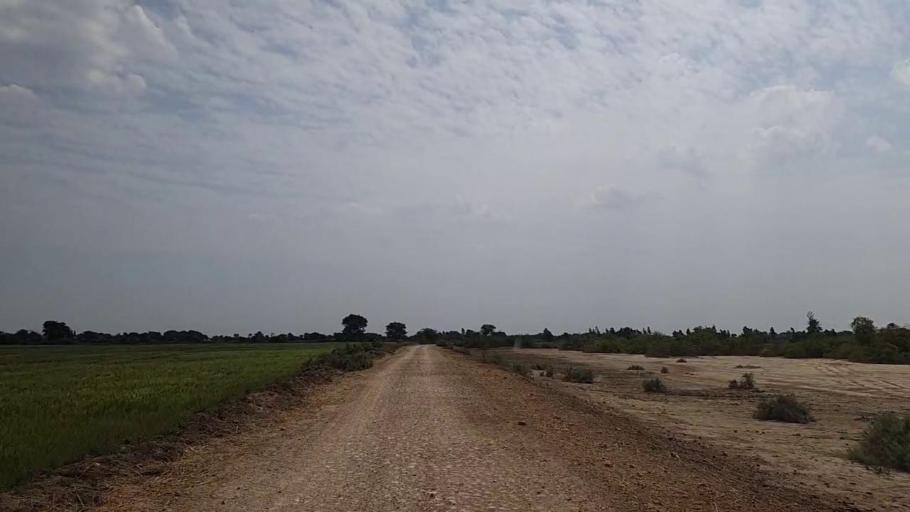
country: PK
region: Sindh
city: Daro Mehar
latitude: 24.8327
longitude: 68.1644
